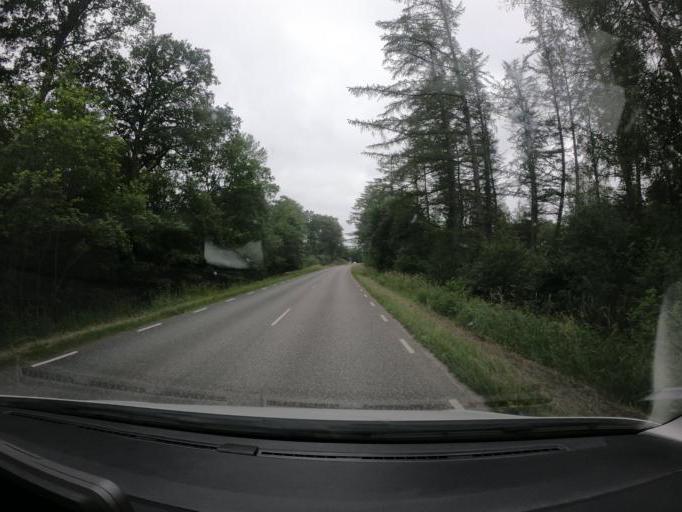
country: SE
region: Skane
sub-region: Perstorps Kommun
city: Perstorp
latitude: 56.1215
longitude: 13.4057
